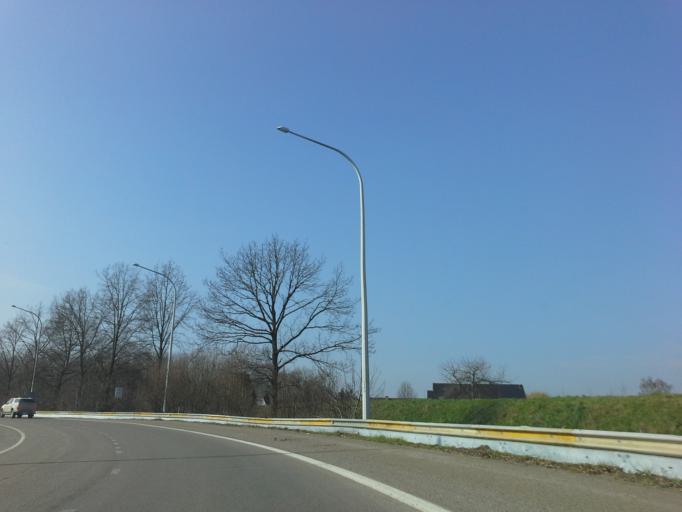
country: BE
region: Flanders
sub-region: Provincie Limburg
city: Bilzen
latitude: 50.8630
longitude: 5.5018
